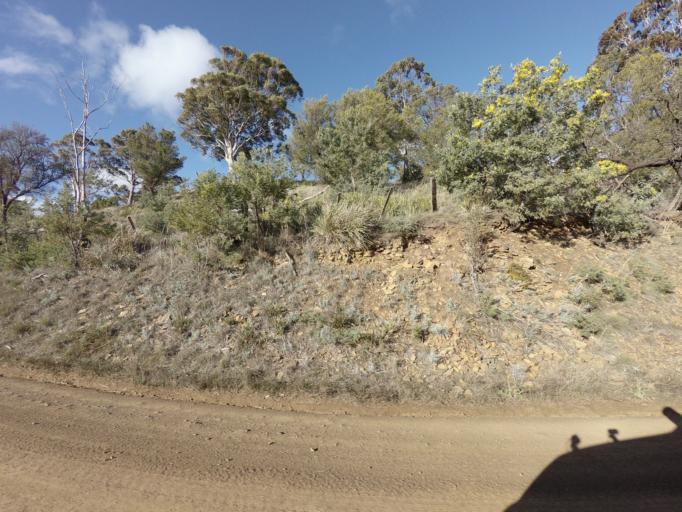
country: AU
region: Tasmania
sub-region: Derwent Valley
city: New Norfolk
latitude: -42.7033
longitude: 146.9969
